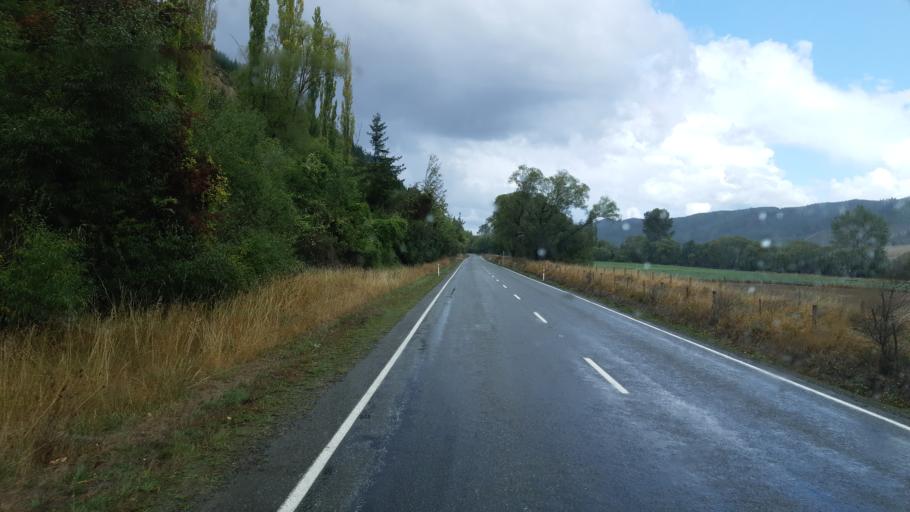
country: NZ
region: Tasman
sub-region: Tasman District
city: Wakefield
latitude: -41.4627
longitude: 172.8392
